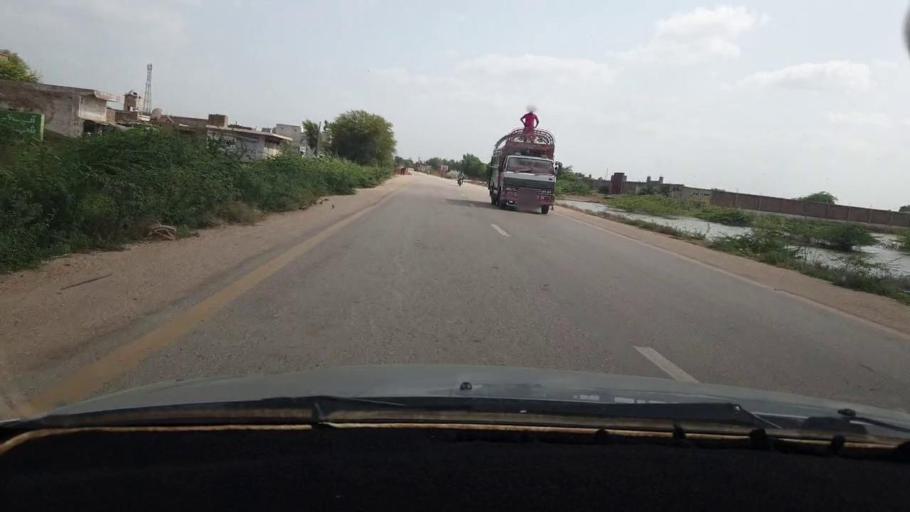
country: PK
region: Sindh
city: Naukot
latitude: 24.9796
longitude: 69.2942
